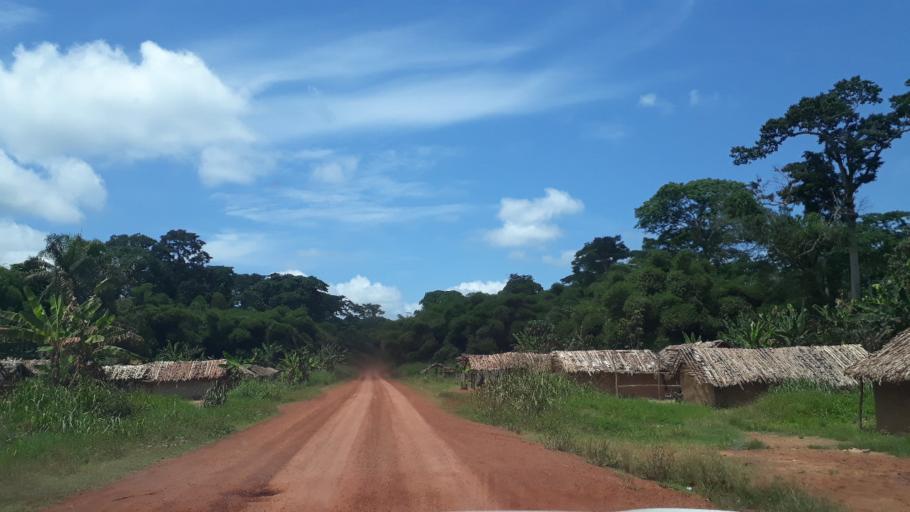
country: CD
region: Eastern Province
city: Kisangani
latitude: 0.5652
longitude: 25.8606
